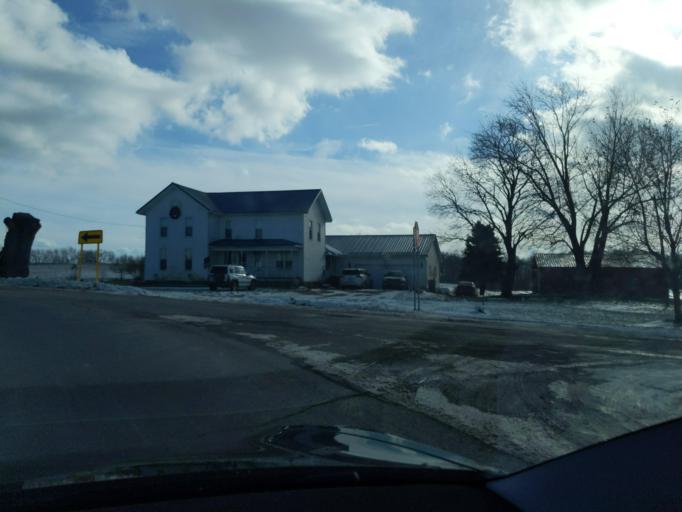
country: US
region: Michigan
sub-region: Ingham County
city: Stockbridge
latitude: 42.4824
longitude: -84.0891
